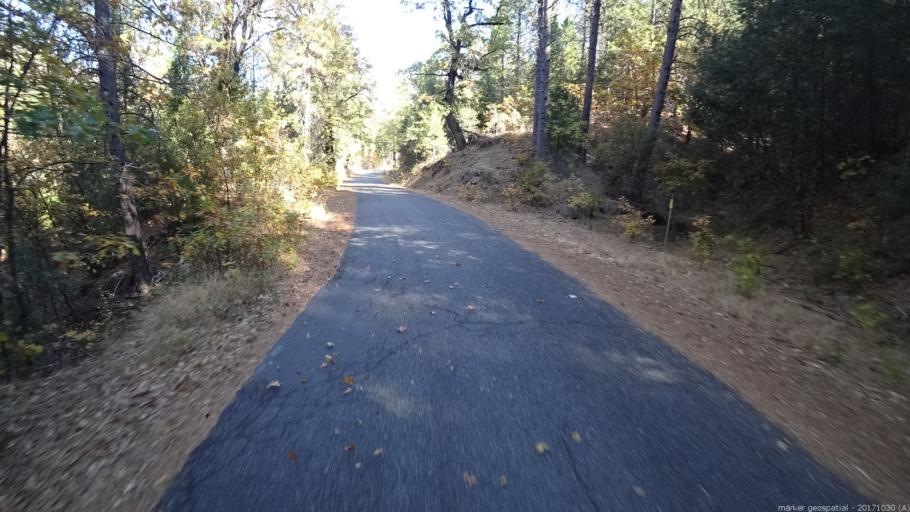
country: US
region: California
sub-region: Shasta County
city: Shingletown
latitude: 40.5593
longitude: -121.9031
